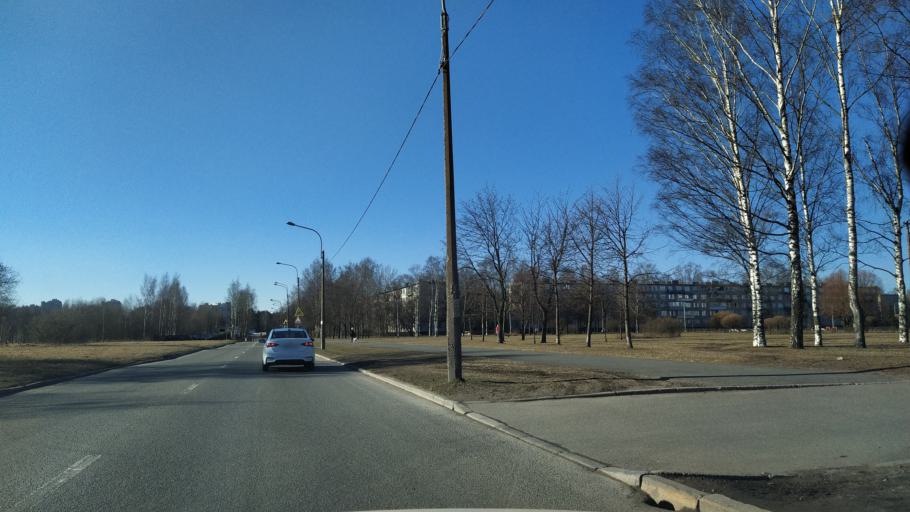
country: RU
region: Leningrad
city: Akademicheskoe
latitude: 59.9995
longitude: 30.4275
